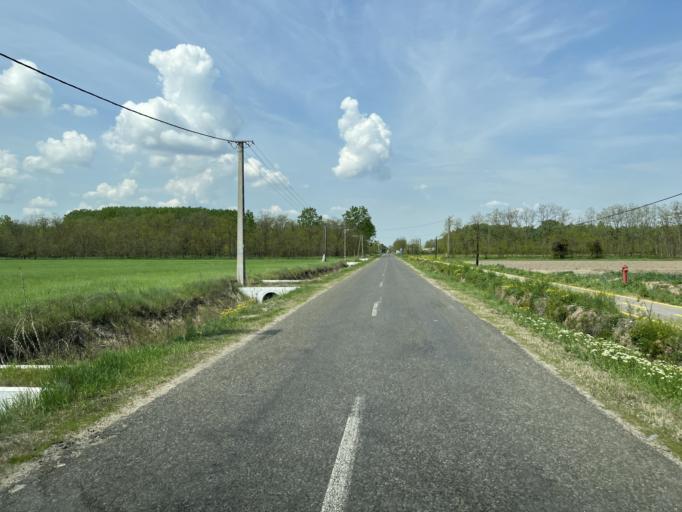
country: HU
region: Pest
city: Nagykoros
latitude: 47.0981
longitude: 19.8133
